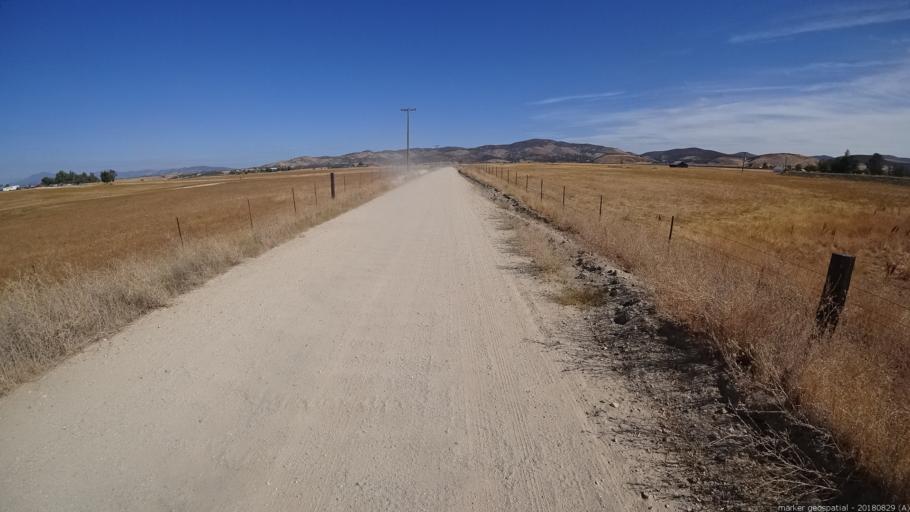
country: US
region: California
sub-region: Monterey County
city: King City
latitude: 35.9559
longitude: -121.0998
